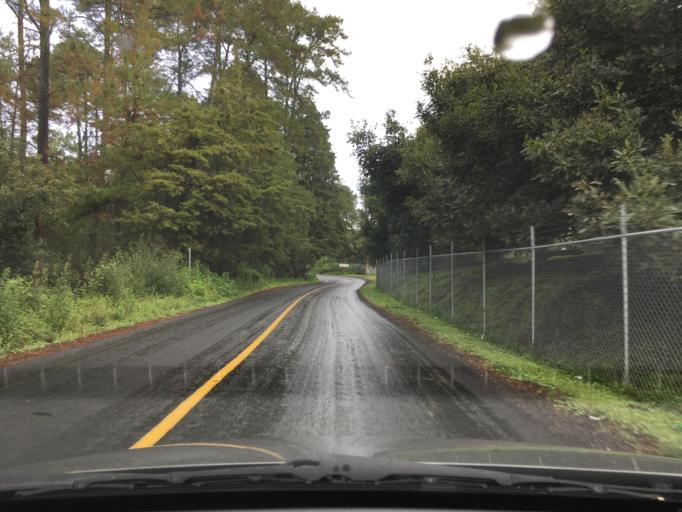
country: MX
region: Michoacan
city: Nuevo San Juan Parangaricutiro
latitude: 19.4340
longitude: -102.1466
